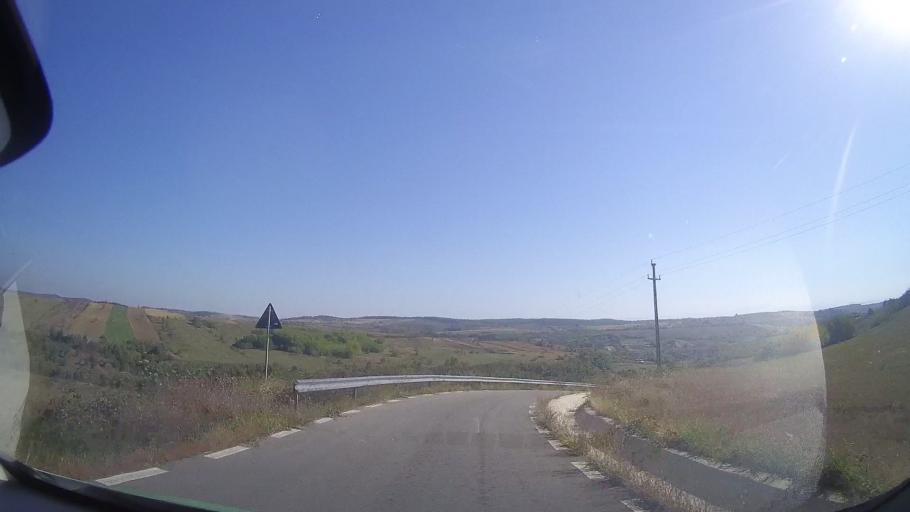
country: RO
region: Timis
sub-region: Comuna Ohaba Lunga
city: Ohaba Lunga
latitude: 45.9109
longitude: 21.9694
